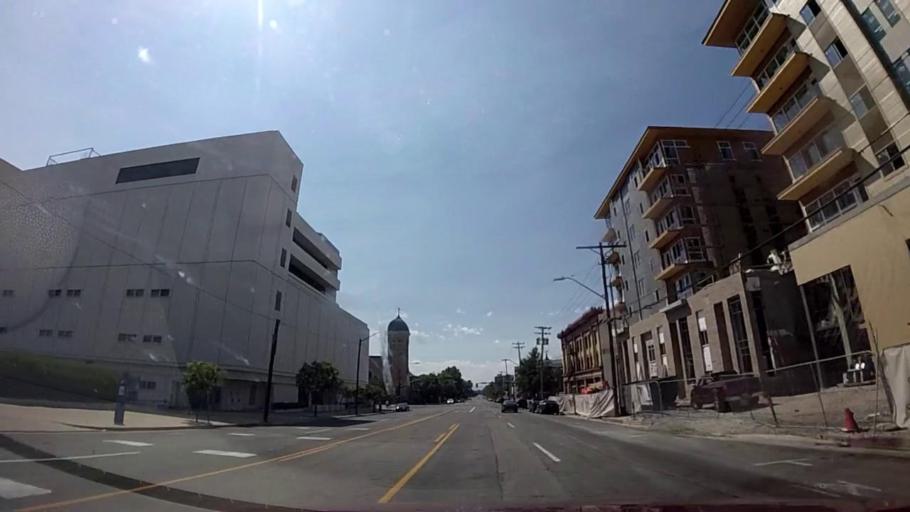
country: US
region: Utah
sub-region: Salt Lake County
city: Salt Lake City
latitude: 40.7658
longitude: -111.8854
